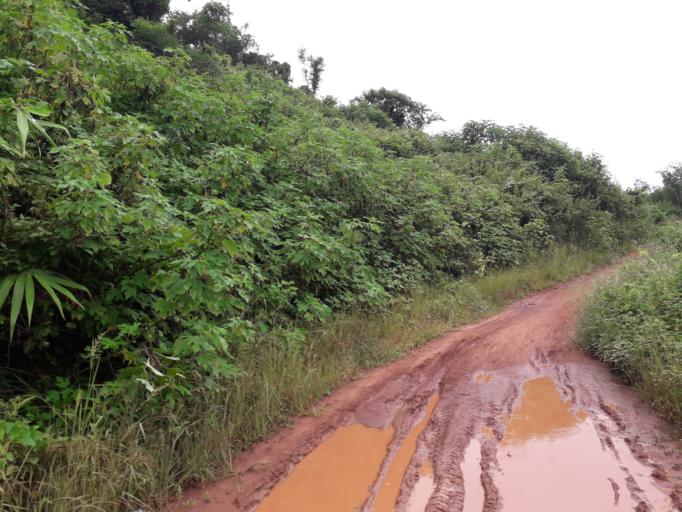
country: CN
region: Yunnan
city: Menglie
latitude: 22.2413
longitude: 101.6130
